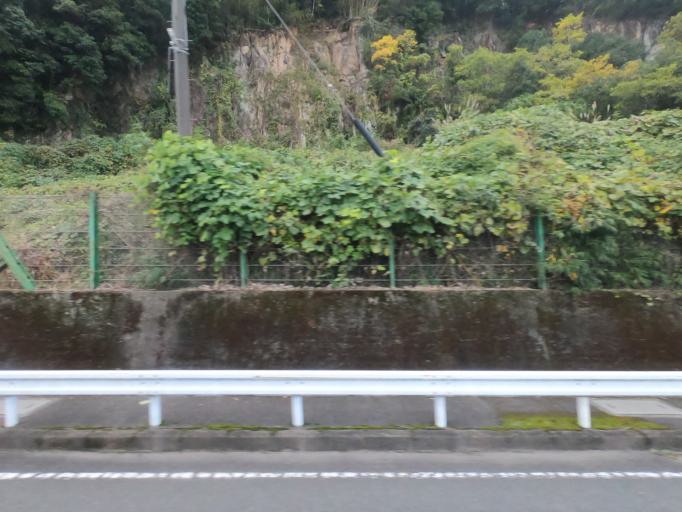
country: JP
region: Kumamoto
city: Minamata
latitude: 32.2659
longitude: 130.5067
